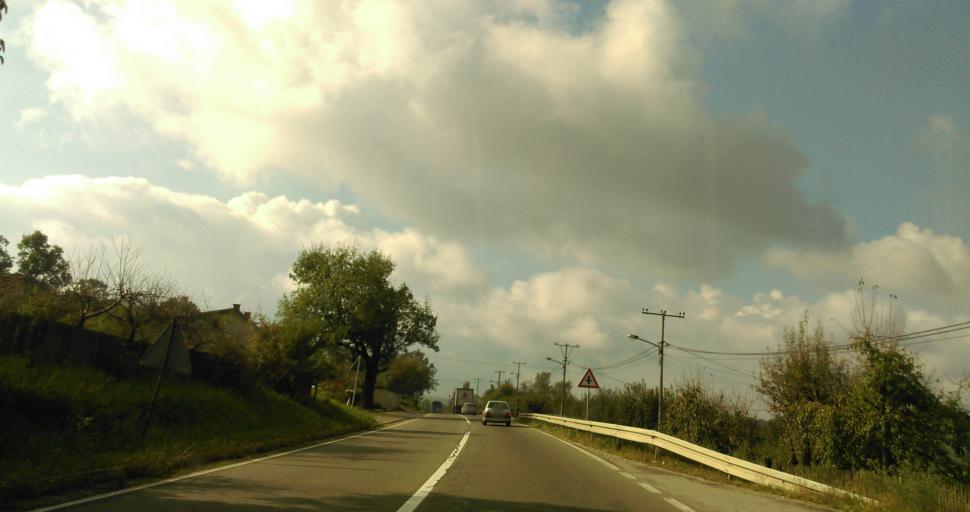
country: RS
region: Central Serbia
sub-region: Kolubarski Okrug
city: Lajkovac
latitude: 44.3629
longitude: 20.1927
